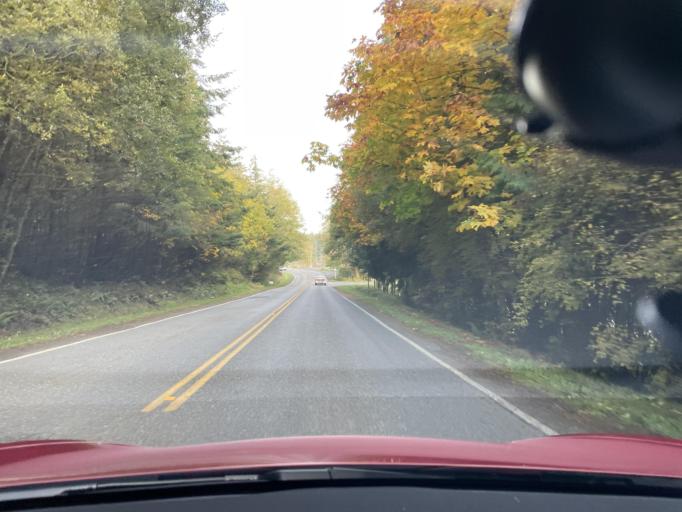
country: US
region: Washington
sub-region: San Juan County
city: Friday Harbor
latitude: 48.5386
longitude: -123.0329
